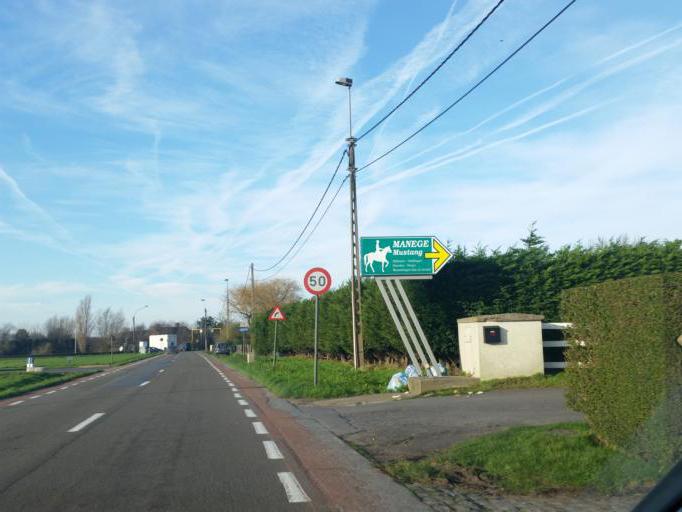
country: BE
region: Flanders
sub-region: Provincie West-Vlaanderen
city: De Haan
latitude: 51.2687
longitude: 3.0523
